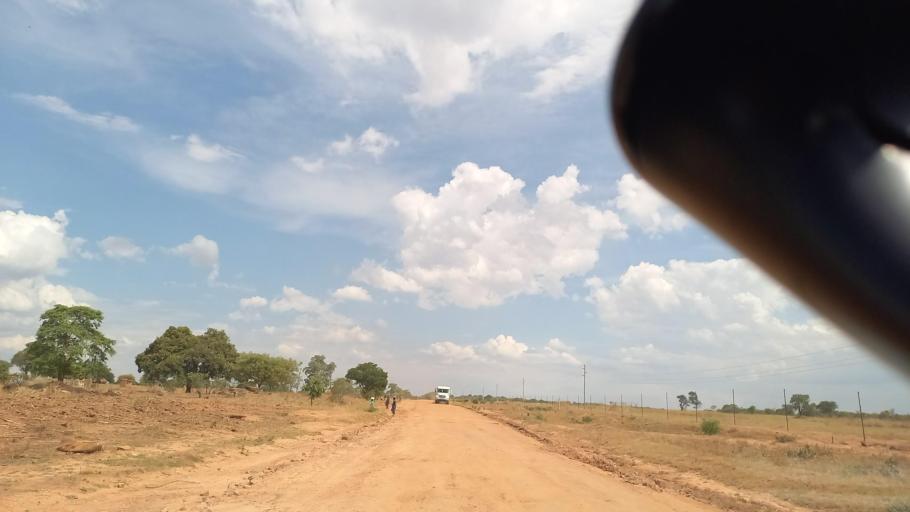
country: ZM
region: Southern
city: Nakambala
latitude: -16.1117
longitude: 28.0285
